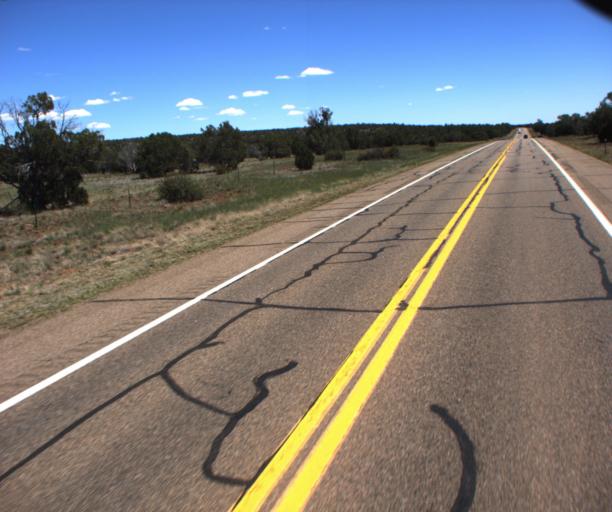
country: US
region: Arizona
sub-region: Yavapai County
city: Paulden
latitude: 35.1178
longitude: -112.4334
